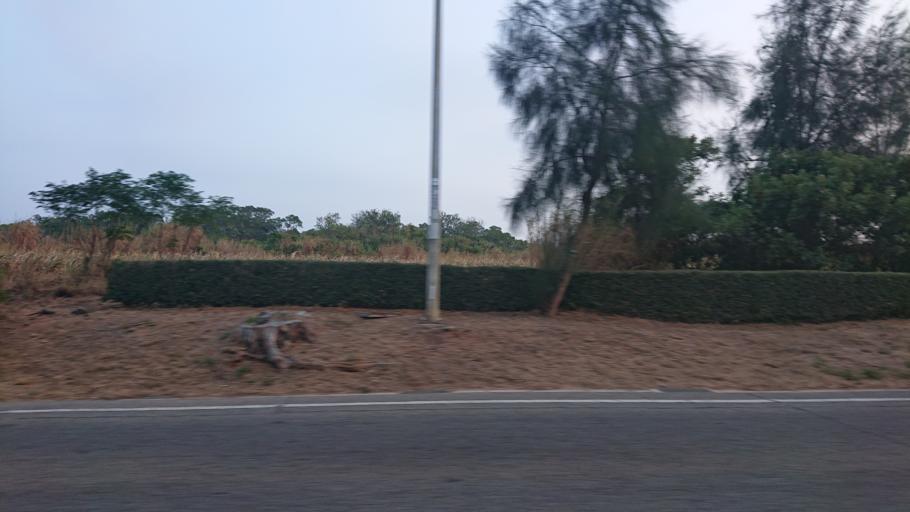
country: TW
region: Fukien
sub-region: Kinmen
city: Jincheng
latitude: 24.4536
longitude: 118.3587
